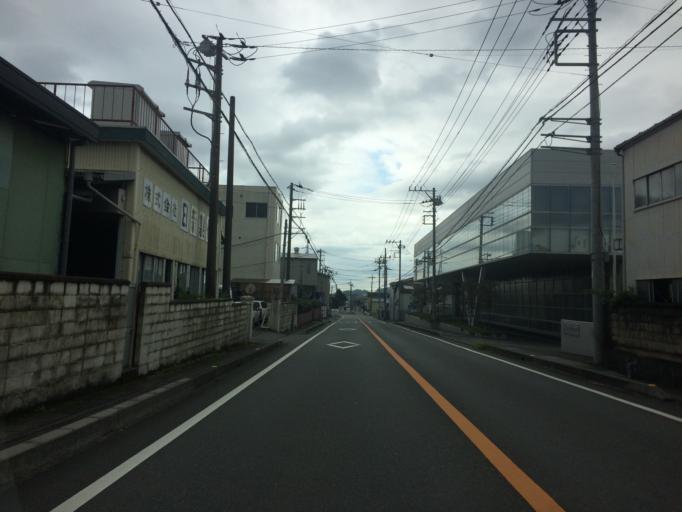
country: JP
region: Shizuoka
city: Fuji
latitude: 35.1827
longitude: 138.6484
